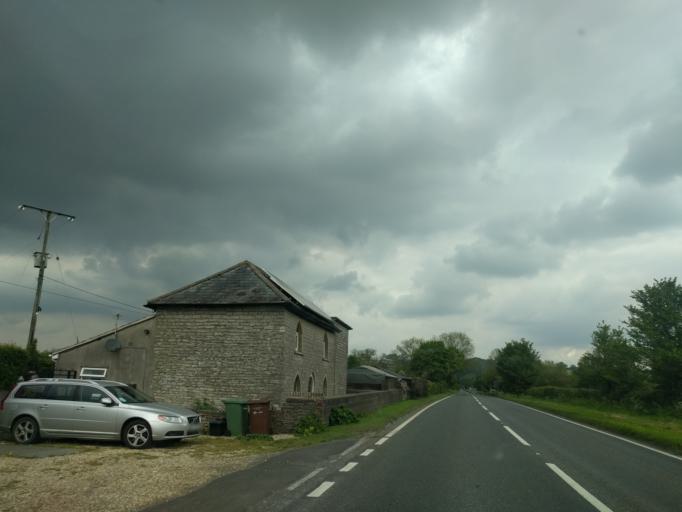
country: GB
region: England
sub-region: Somerset
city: Castle Cary
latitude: 51.1189
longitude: -2.5783
